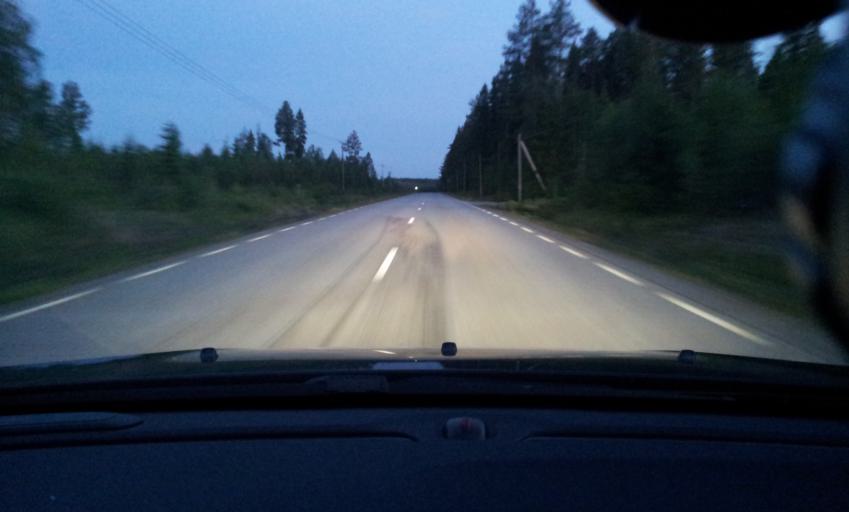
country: SE
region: Jaemtland
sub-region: OEstersunds Kommun
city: Brunflo
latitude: 62.7330
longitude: 14.9785
